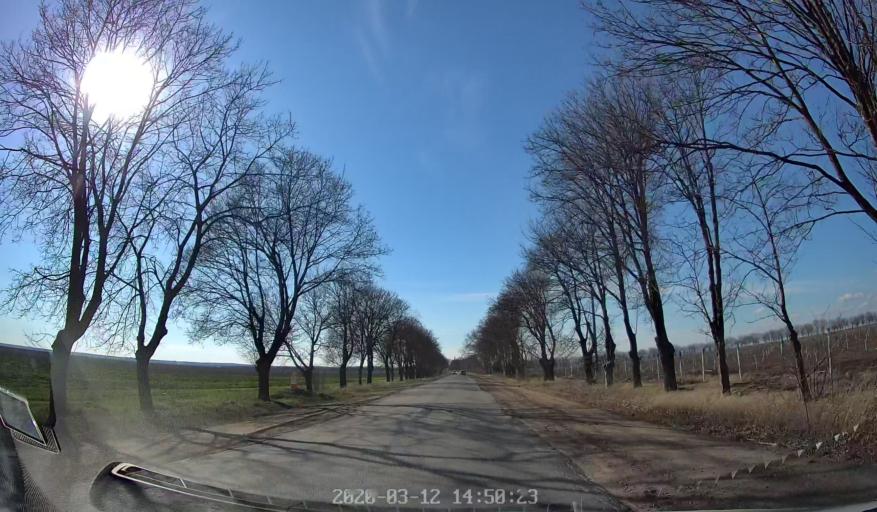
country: MD
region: Criuleni
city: Criuleni
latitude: 47.2229
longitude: 29.1310
